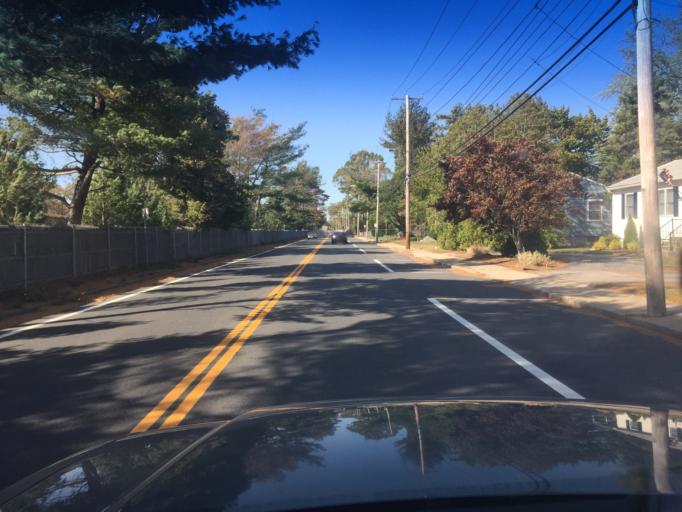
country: US
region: Rhode Island
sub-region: Providence County
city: Pawtucket
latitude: 41.8502
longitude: -71.3568
